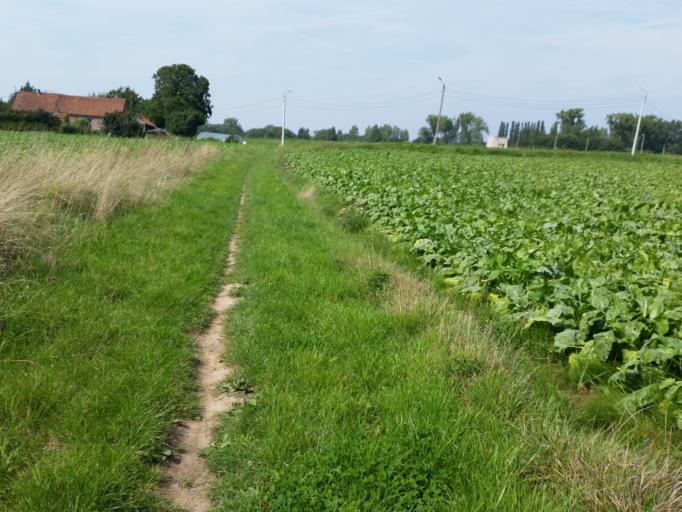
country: BE
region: Flanders
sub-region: Provincie Vlaams-Brabant
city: Zemst
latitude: 50.9644
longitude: 4.4732
